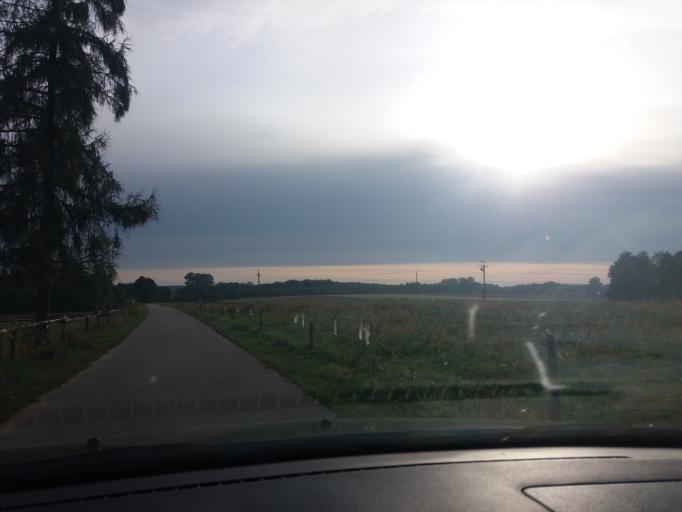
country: PL
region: Masovian Voivodeship
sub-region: Powiat mlawski
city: Wieczfnia Koscielna
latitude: 53.2066
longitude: 20.4493
